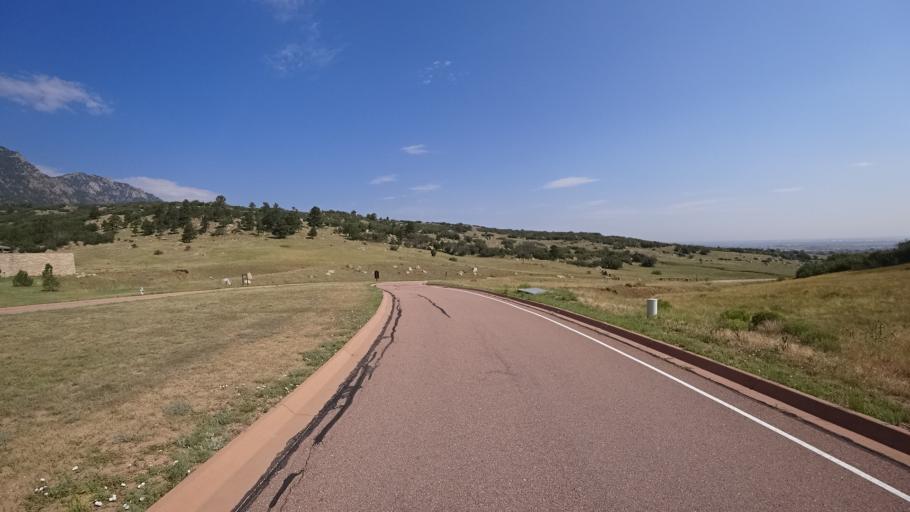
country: US
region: Colorado
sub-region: El Paso County
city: Fort Carson
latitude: 38.7353
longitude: -104.8186
